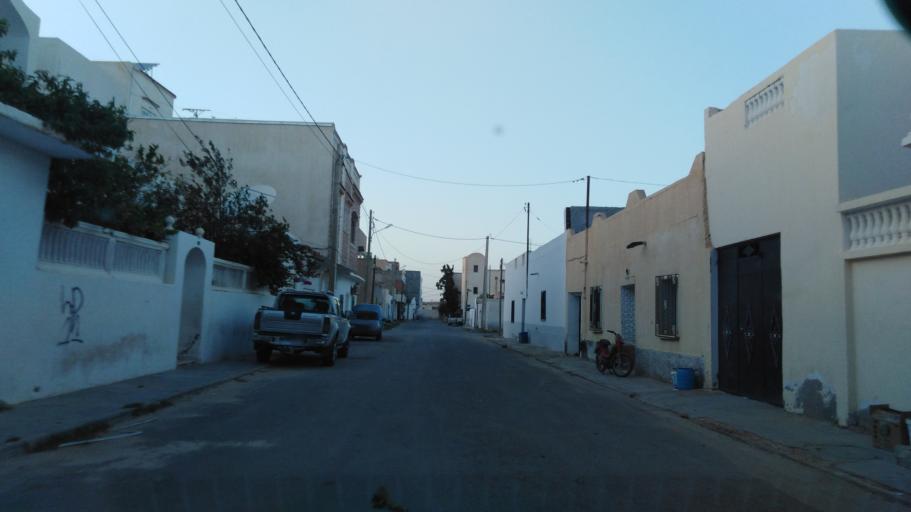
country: TN
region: Tataouine
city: Tataouine
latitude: 32.9364
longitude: 10.4522
